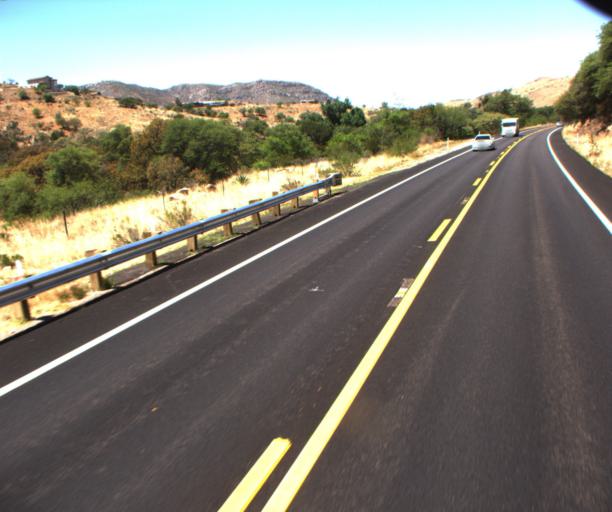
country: US
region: Arizona
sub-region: Cochise County
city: Bisbee
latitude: 31.4884
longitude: -109.9878
